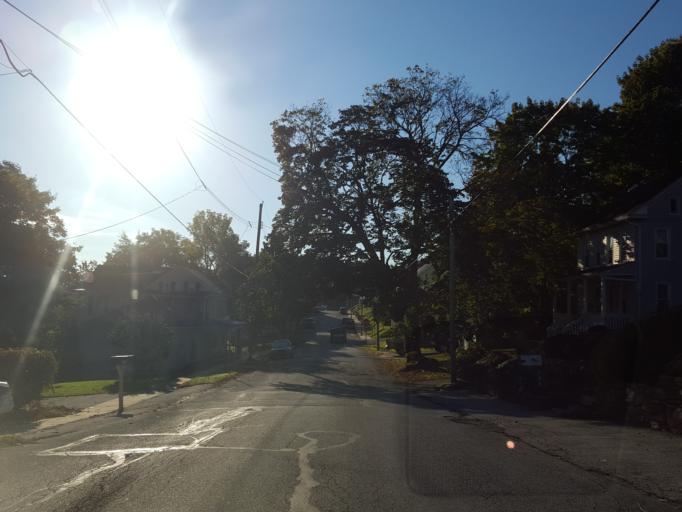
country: US
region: Pennsylvania
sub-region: York County
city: Yoe
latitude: 39.9113
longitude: -76.6401
